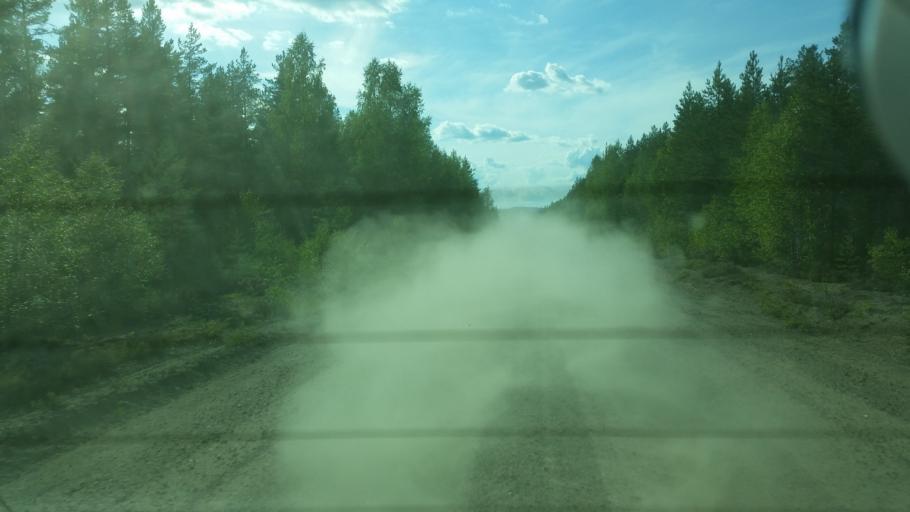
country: SE
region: Vaesternorrland
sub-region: Ange Kommun
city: Ange
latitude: 62.1993
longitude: 15.5744
